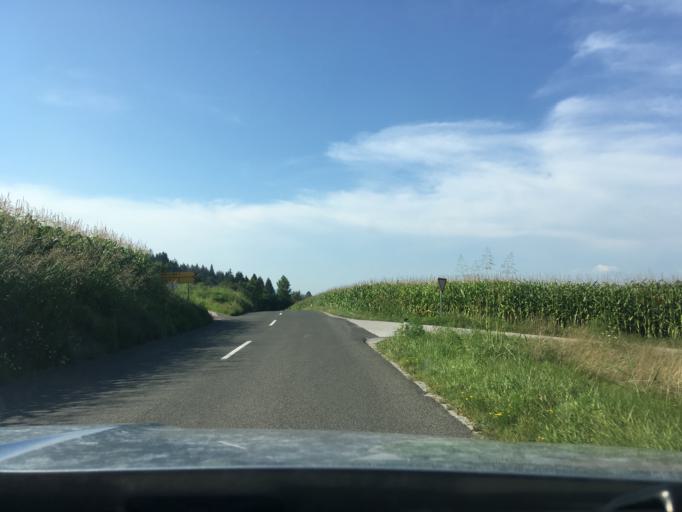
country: SI
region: Crnomelj
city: Crnomelj
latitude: 45.4997
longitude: 15.1913
